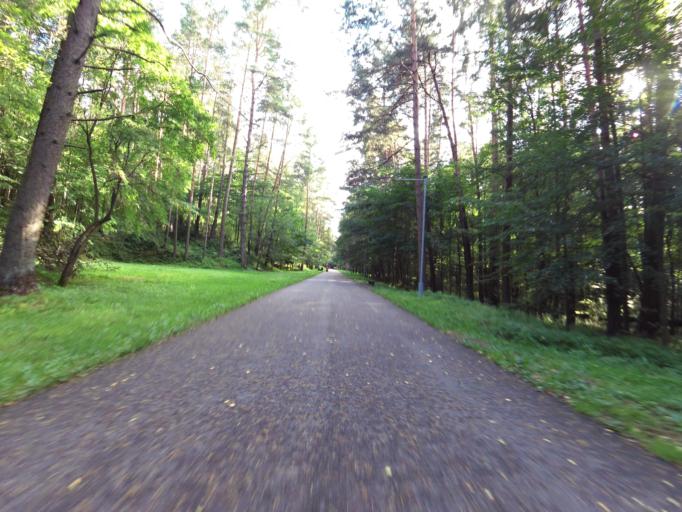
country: LT
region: Vilnius County
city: Vilkpede
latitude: 54.6804
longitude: 25.2410
